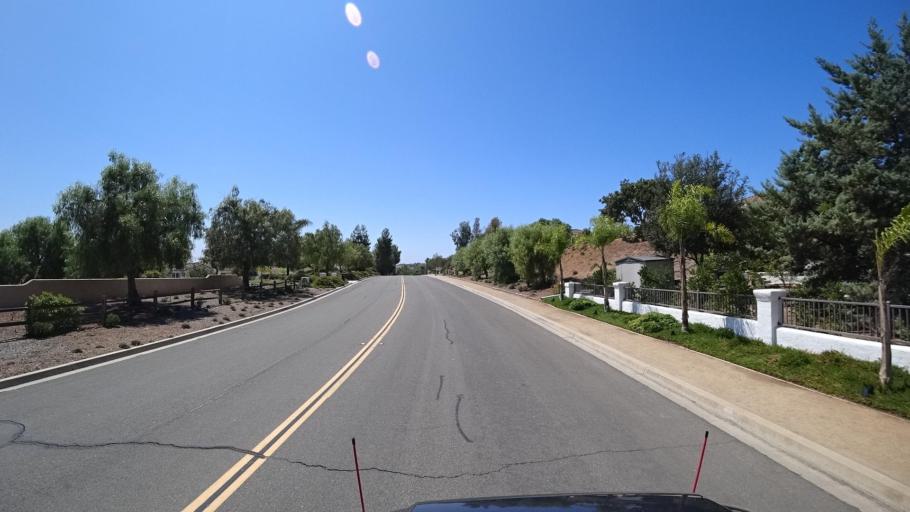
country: US
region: California
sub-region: San Diego County
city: Bonsall
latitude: 33.3273
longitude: -117.1967
